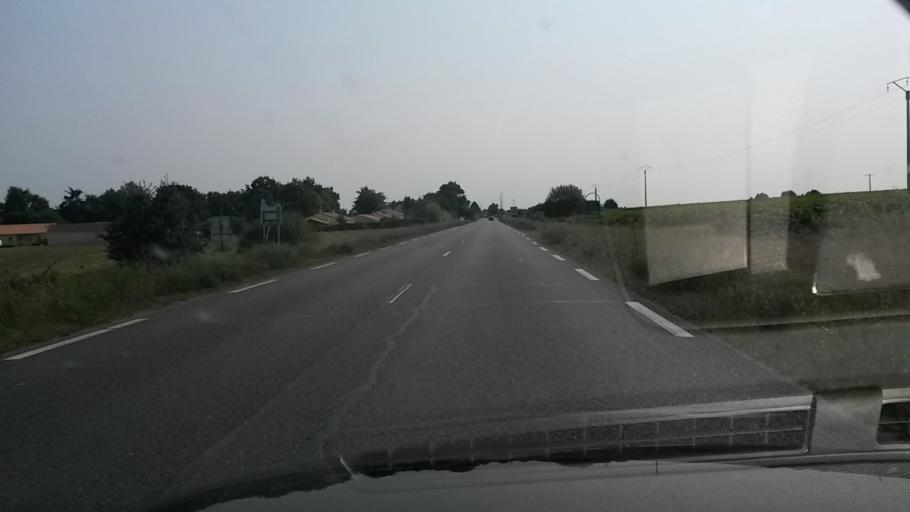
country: FR
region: Pays de la Loire
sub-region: Departement de la Loire-Atlantique
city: Mouzillon
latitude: 47.1487
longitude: -1.2801
